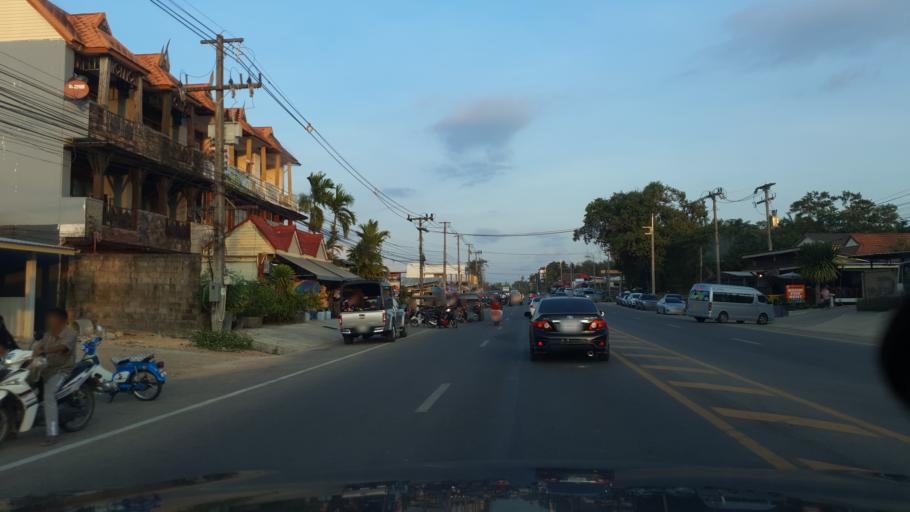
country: TH
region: Phangnga
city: Ban Ao Nang
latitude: 8.0418
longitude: 98.8421
